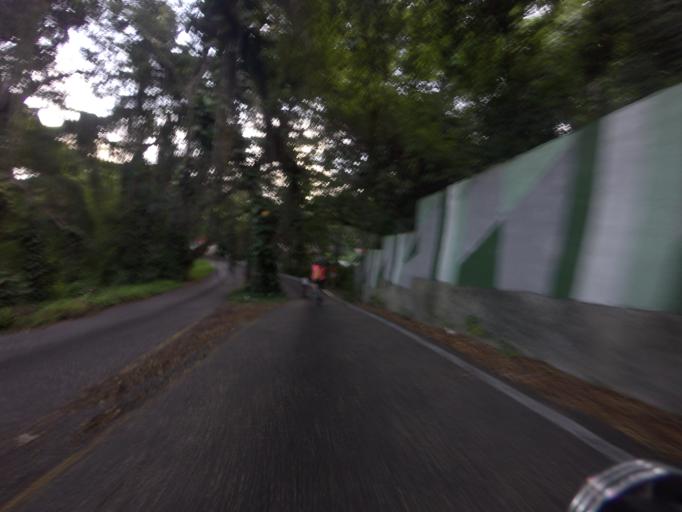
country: CU
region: La Habana
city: Cerro
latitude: 23.1097
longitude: -82.4076
